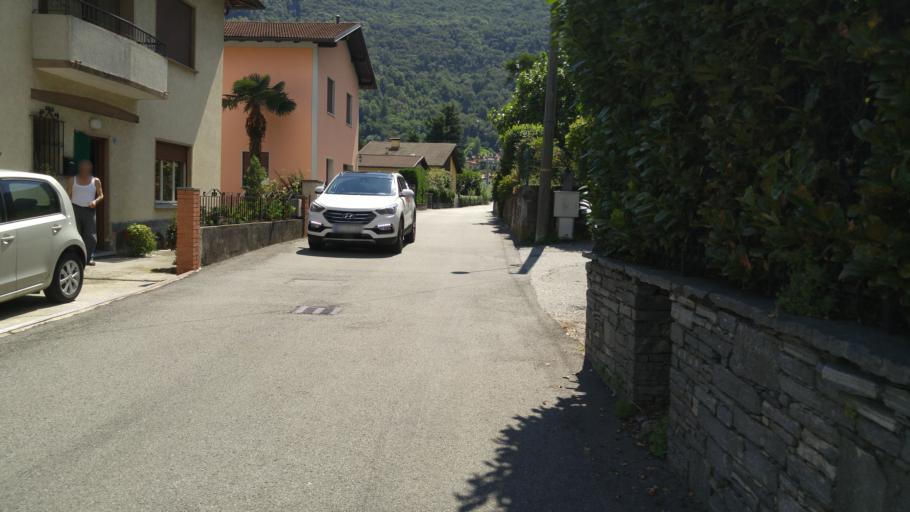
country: IT
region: Piedmont
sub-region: Provincia Verbano-Cusio-Ossola
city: Cannobio
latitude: 46.0621
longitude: 8.6871
